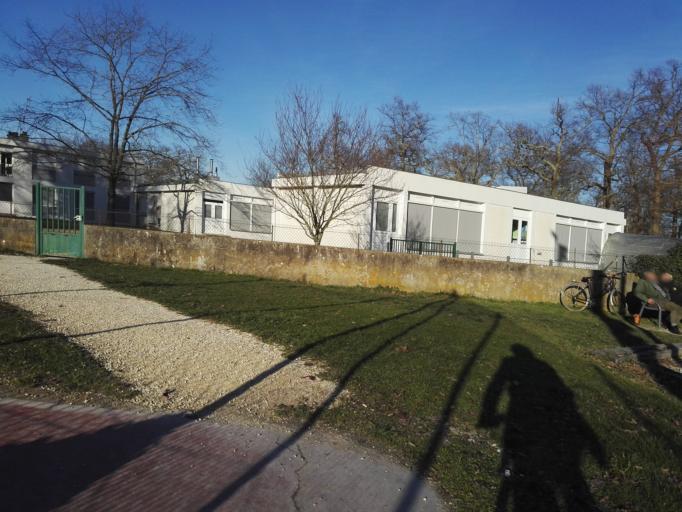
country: FR
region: Aquitaine
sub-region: Departement de la Gironde
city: Pessac
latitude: 44.8173
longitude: -0.6371
